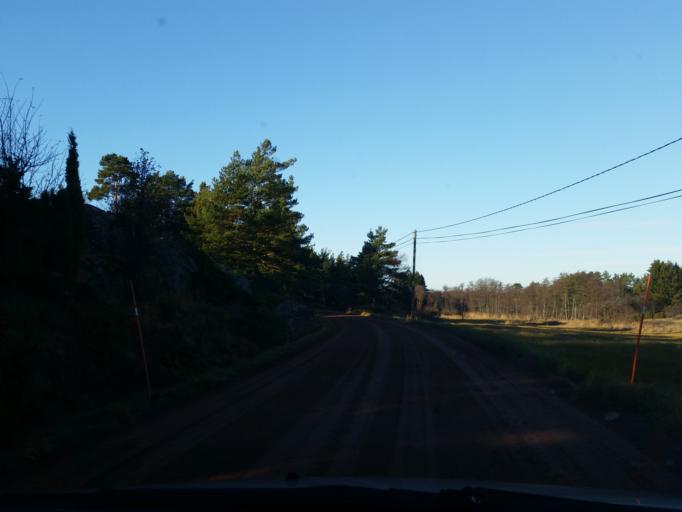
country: AX
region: Alands skaergard
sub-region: Braendoe
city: Braendoe
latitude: 60.4179
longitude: 20.9878
